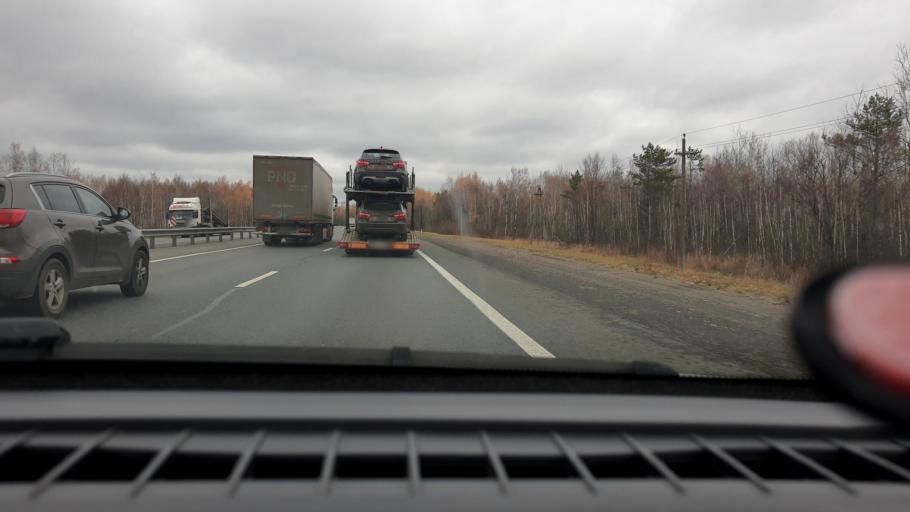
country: RU
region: Nizjnij Novgorod
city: Gorbatovka
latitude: 56.2887
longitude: 43.6979
